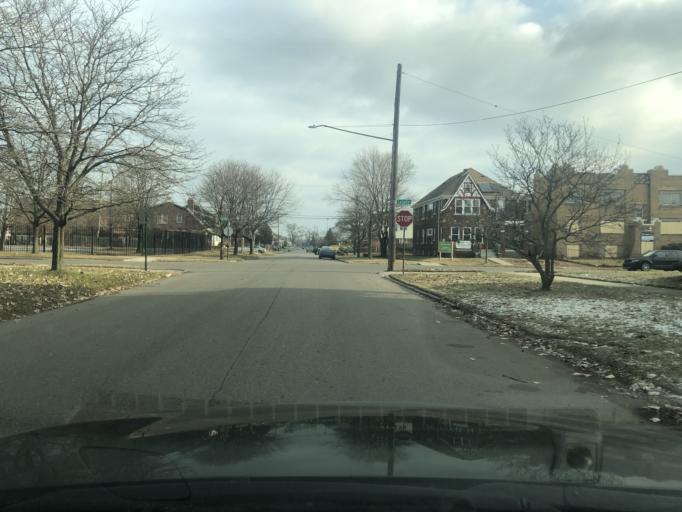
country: US
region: Michigan
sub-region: Wayne County
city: Highland Park
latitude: 42.3983
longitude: -83.1224
